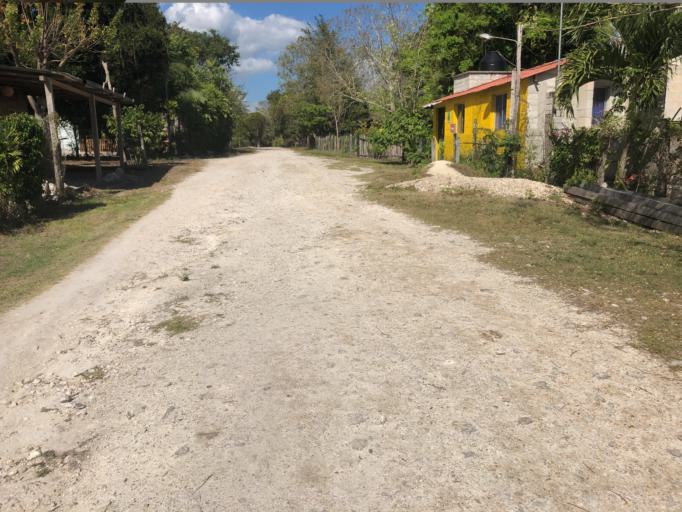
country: MX
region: Quintana Roo
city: Nicolas Bravo
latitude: 18.4531
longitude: -89.3055
